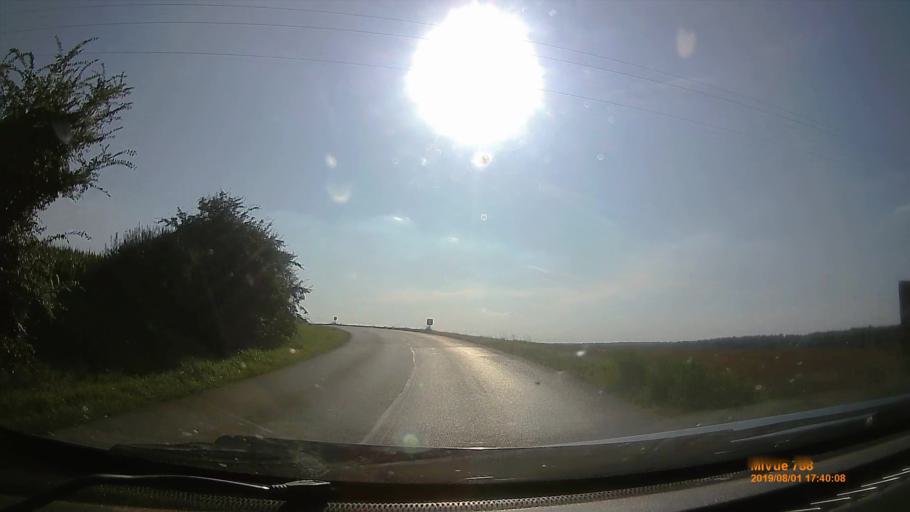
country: HU
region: Baranya
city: Komlo
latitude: 46.2015
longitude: 18.1863
